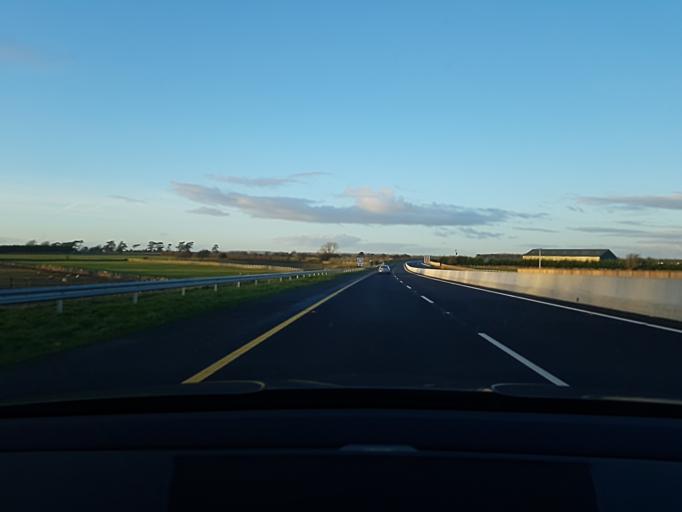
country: IE
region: Connaught
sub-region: County Galway
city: Athenry
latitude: 53.3206
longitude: -8.8023
